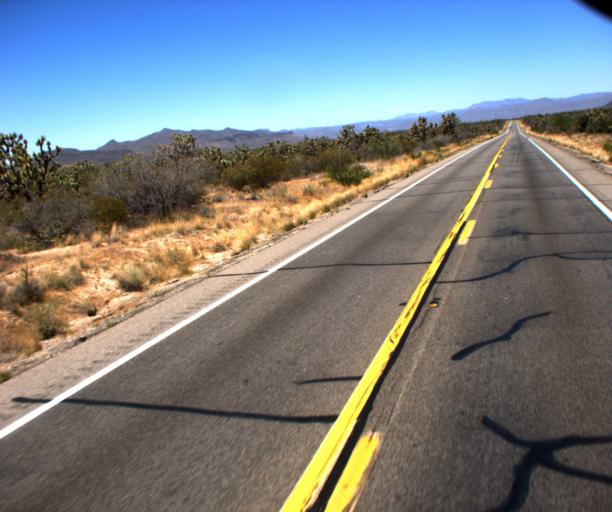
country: US
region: Arizona
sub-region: Yavapai County
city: Congress
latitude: 34.2564
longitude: -113.0855
